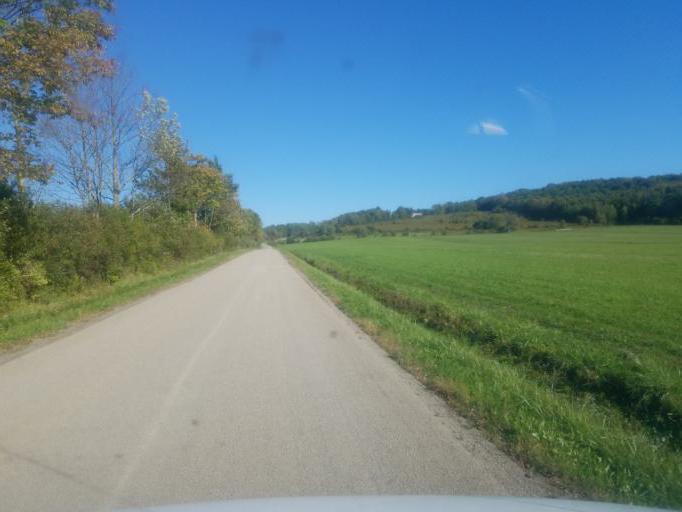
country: US
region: New York
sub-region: Allegany County
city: Cuba
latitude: 42.2338
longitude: -78.2421
